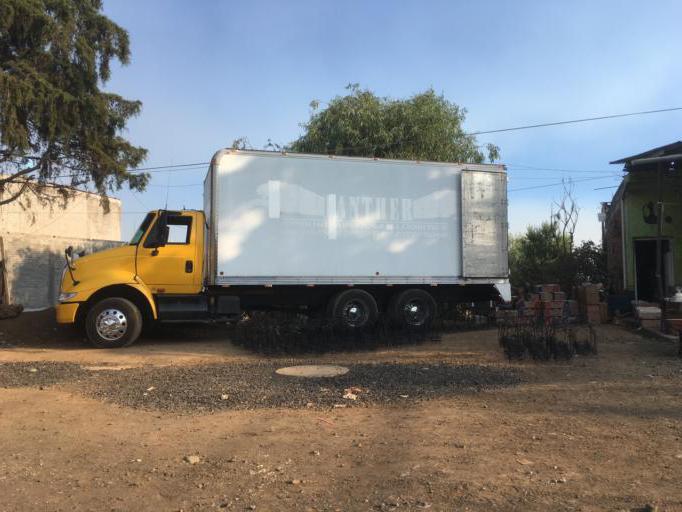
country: MX
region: Michoacan
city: Santa Fe de la Laguna
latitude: 19.6713
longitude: -101.5568
